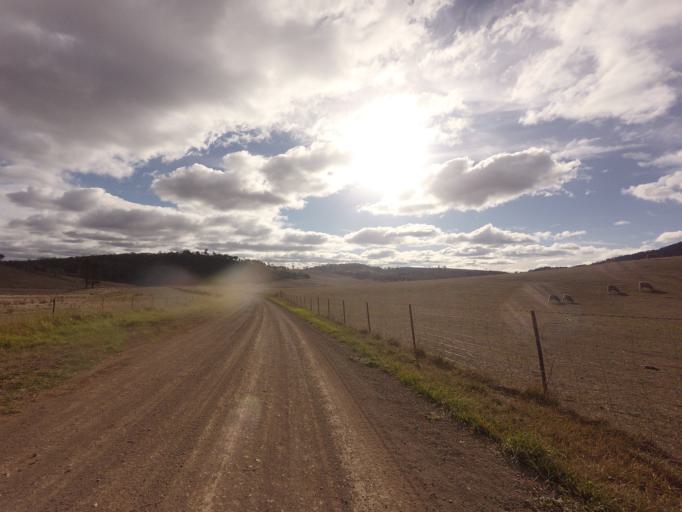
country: AU
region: Tasmania
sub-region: Brighton
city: Bridgewater
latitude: -42.4697
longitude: 147.2815
